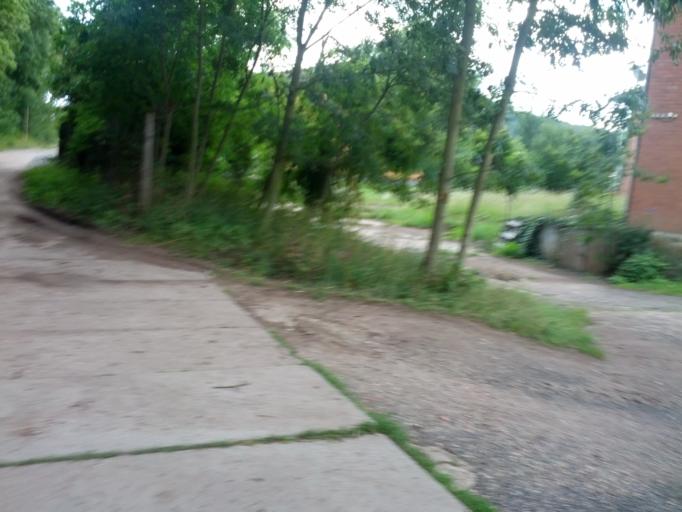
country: DE
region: Thuringia
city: Eisenach
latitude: 50.9829
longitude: 10.3040
